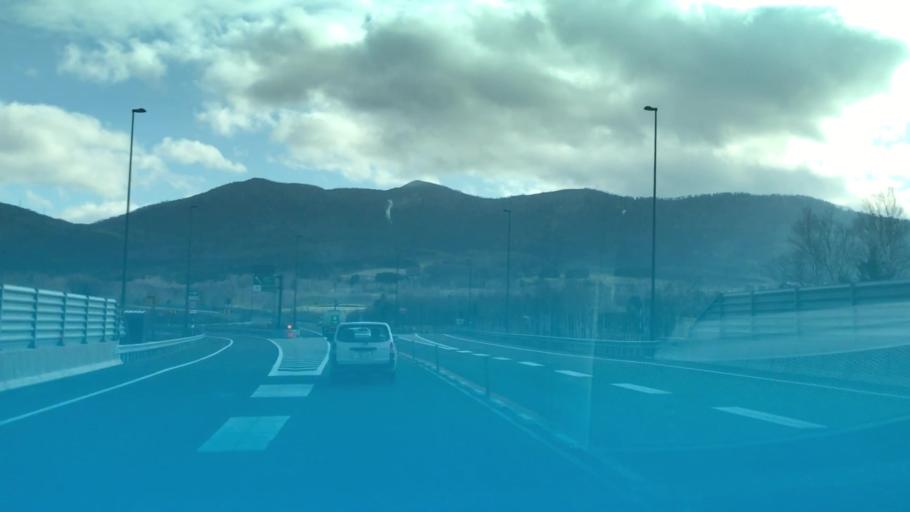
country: JP
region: Hokkaido
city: Shimo-furano
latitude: 43.0443
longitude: 142.6591
